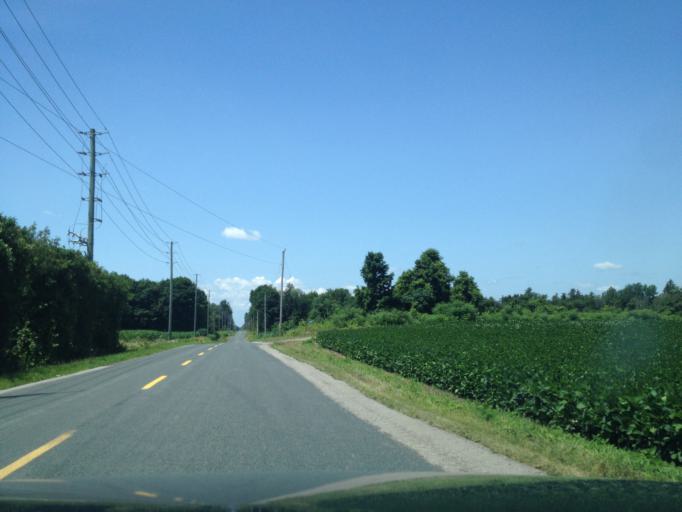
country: CA
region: Ontario
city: Aylmer
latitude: 42.6432
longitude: -80.7396
